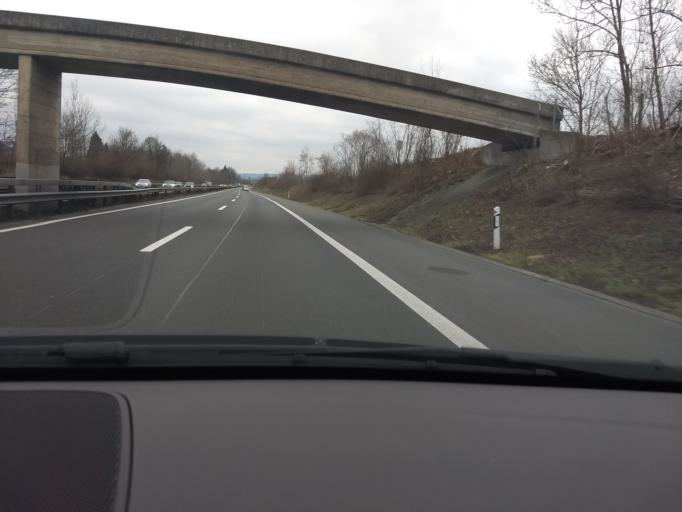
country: CH
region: Lucerne
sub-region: Sursee District
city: Schenkon
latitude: 47.1708
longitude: 8.1369
